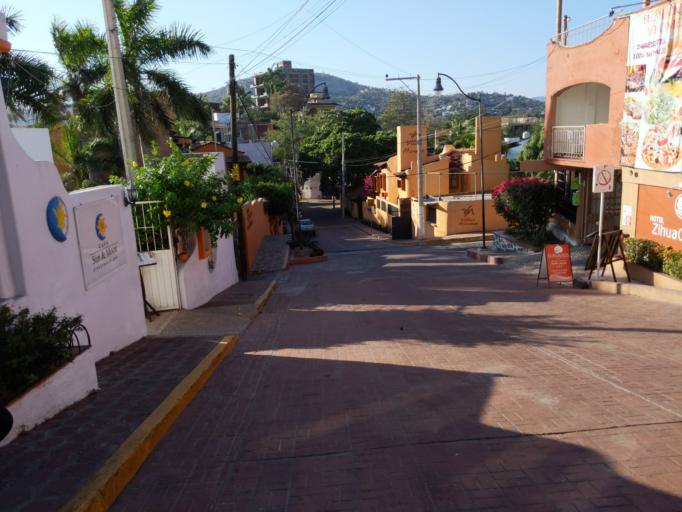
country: MX
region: Guerrero
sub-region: Zihuatanejo de Azueta
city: Ixtapa-Zihuatanejo
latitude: 17.6386
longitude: -101.5503
